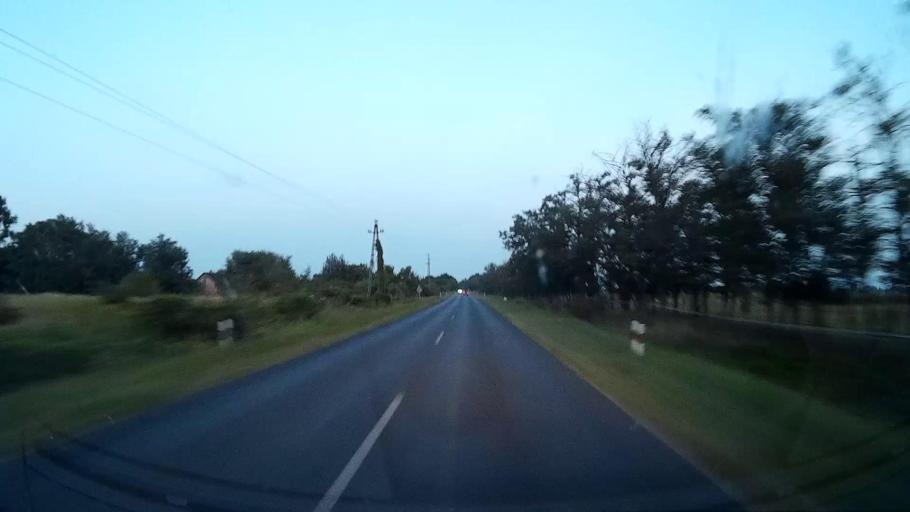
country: HU
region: Pest
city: Cegled
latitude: 47.1896
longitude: 19.7381
